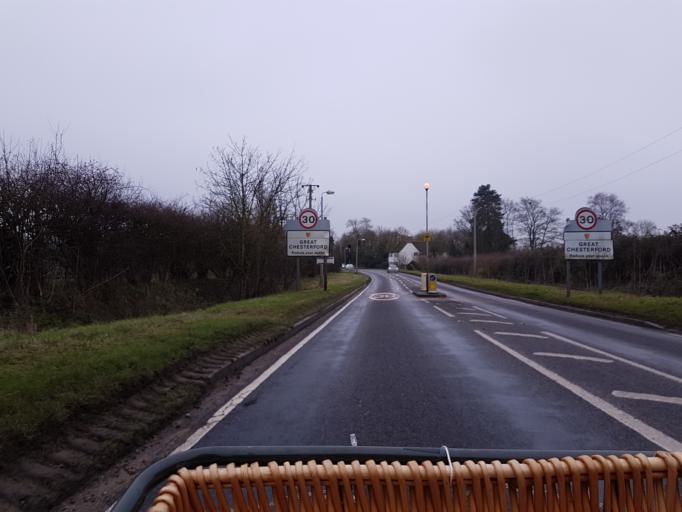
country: GB
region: England
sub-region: Cambridgeshire
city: Duxford
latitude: 52.0679
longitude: 0.1925
